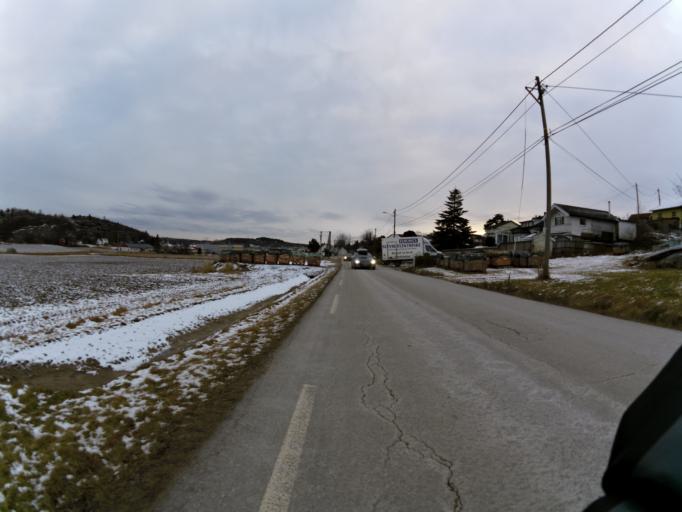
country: NO
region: Ostfold
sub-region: Fredrikstad
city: Fredrikstad
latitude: 59.2153
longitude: 10.8906
